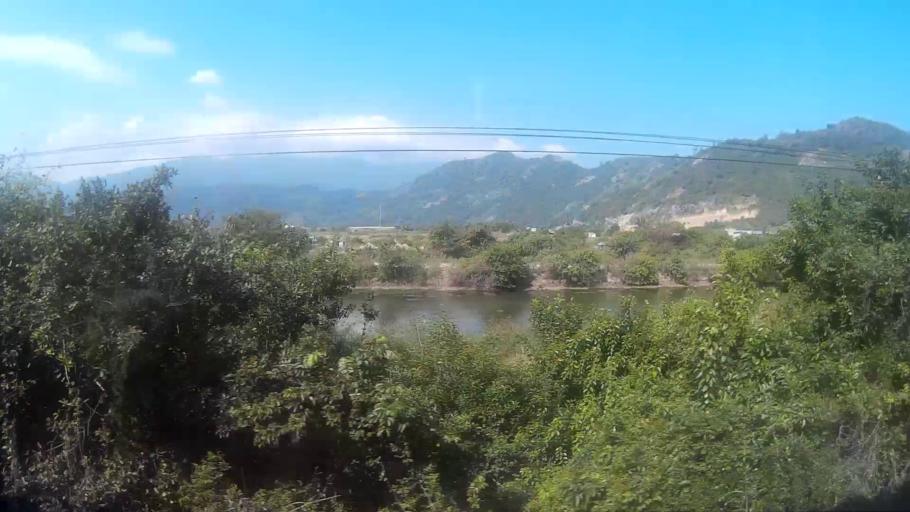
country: VN
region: Khanh Hoa
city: Ninh Hoa
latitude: 12.4086
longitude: 109.1501
